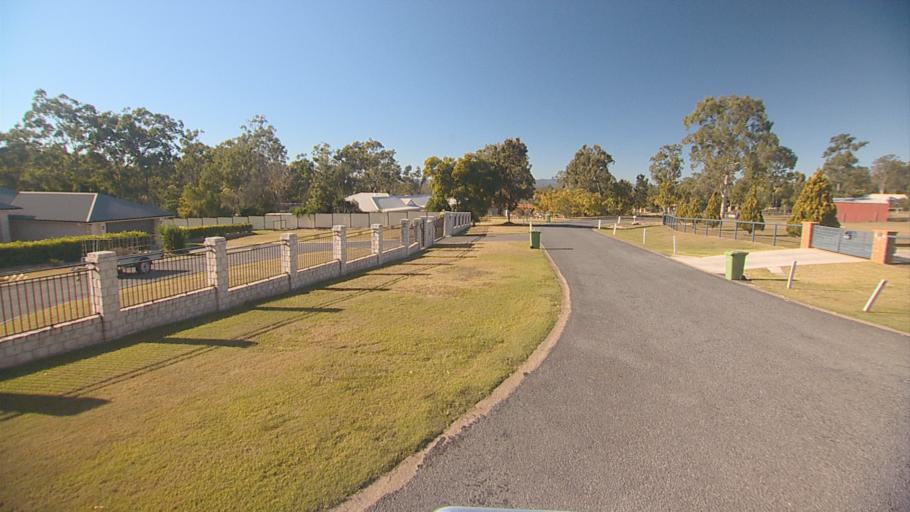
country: AU
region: Queensland
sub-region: Logan
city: North Maclean
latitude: -27.7404
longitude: 152.9617
